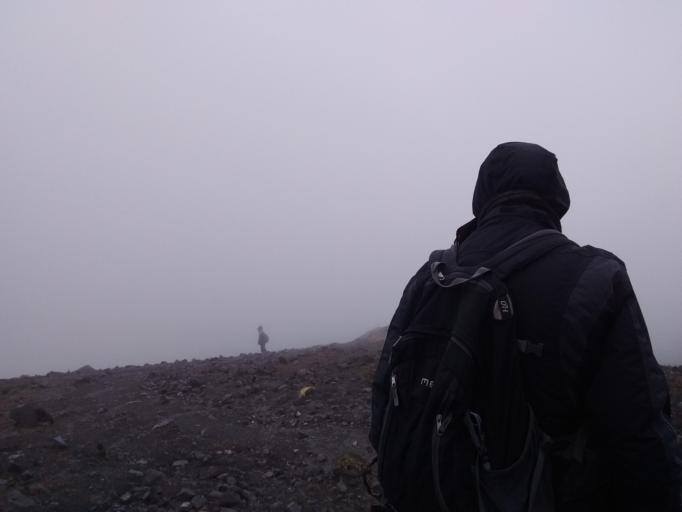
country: CO
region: Cauca
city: Totoro
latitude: 2.3245
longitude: -76.3951
